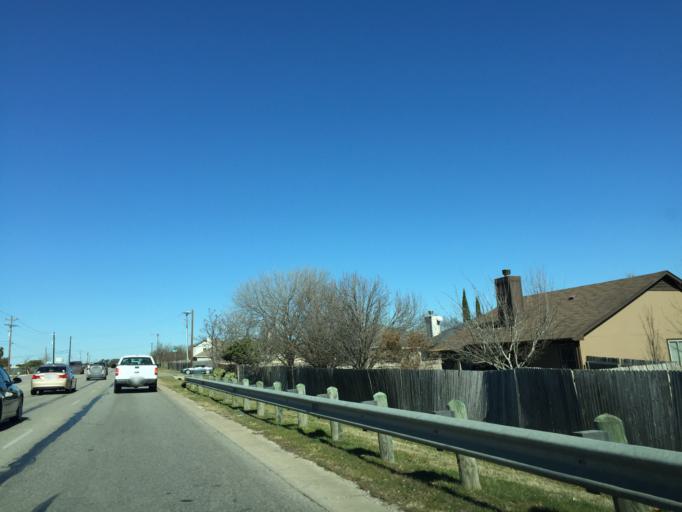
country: US
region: Texas
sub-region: Williamson County
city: Leander
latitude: 30.5609
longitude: -97.8619
